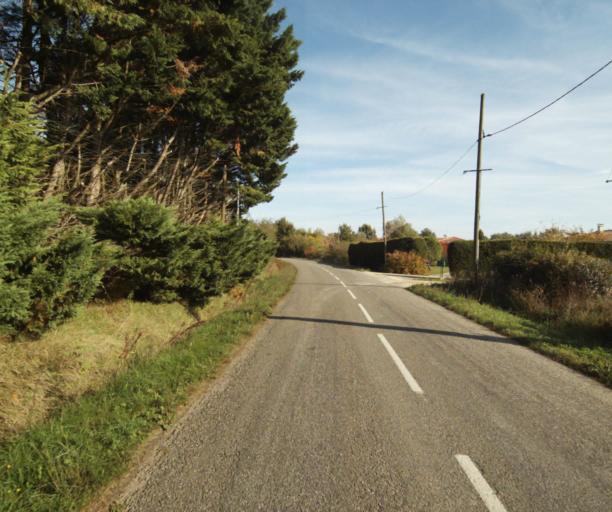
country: FR
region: Midi-Pyrenees
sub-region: Departement du Tarn-et-Garonne
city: Nohic
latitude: 43.9201
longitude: 1.4624
